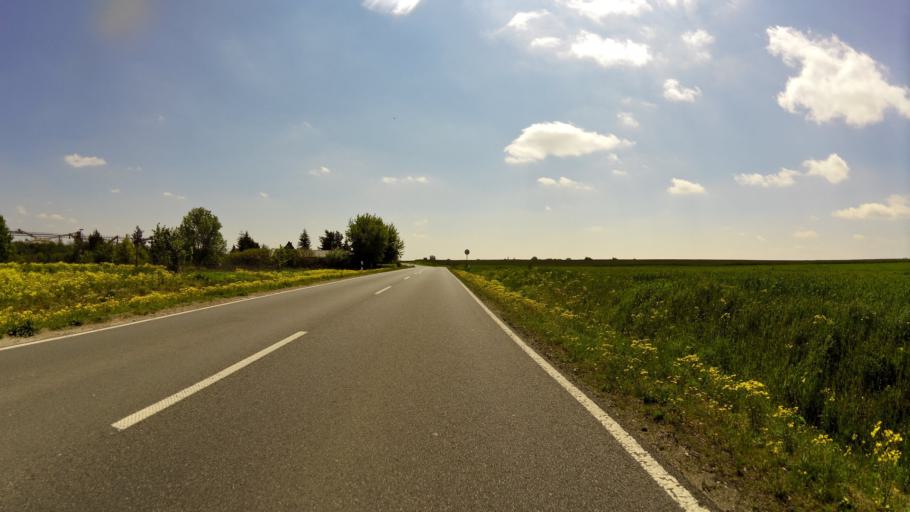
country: DE
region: Saxony
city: Belgern
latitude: 51.4525
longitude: 13.1634
